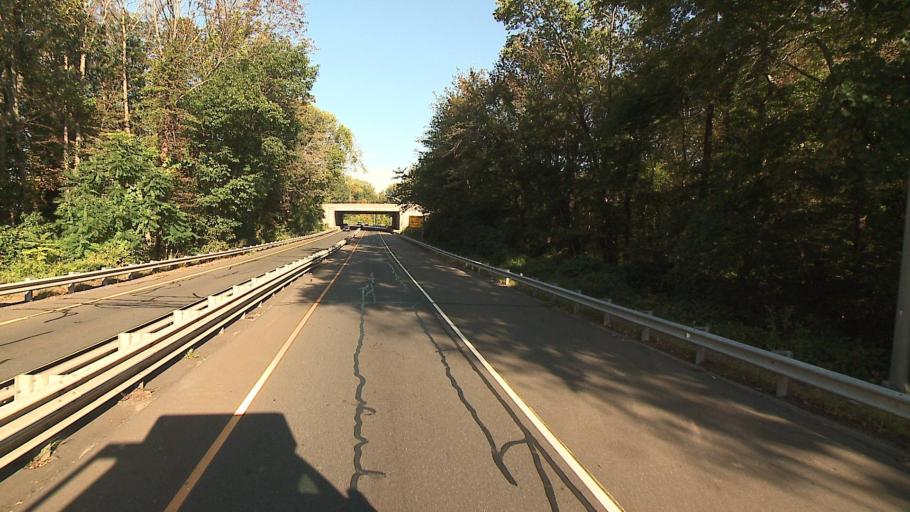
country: US
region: Connecticut
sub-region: New Haven County
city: City of Milford (balance)
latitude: 41.2459
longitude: -73.0841
